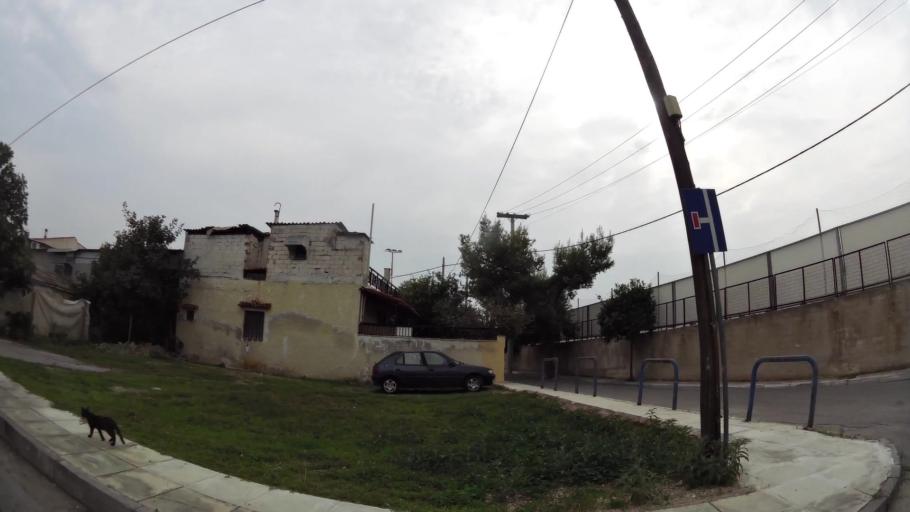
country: GR
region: Attica
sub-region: Nomarchia Athinas
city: Tavros
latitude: 37.9711
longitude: 23.6846
